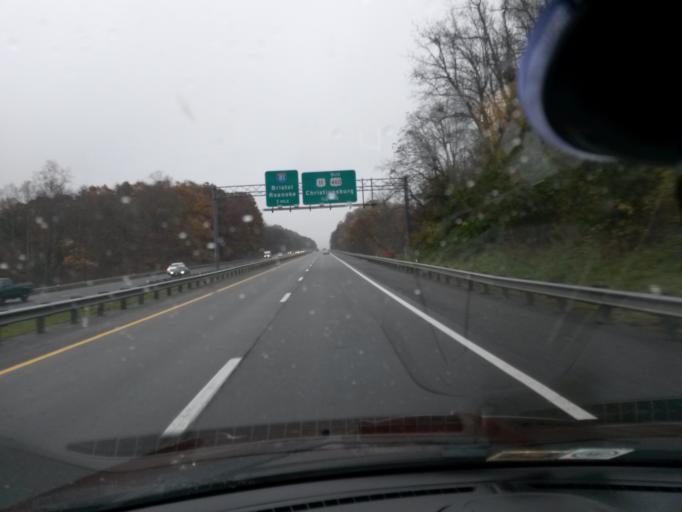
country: US
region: Virginia
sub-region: Montgomery County
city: Christiansburg
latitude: 37.1442
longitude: -80.3898
